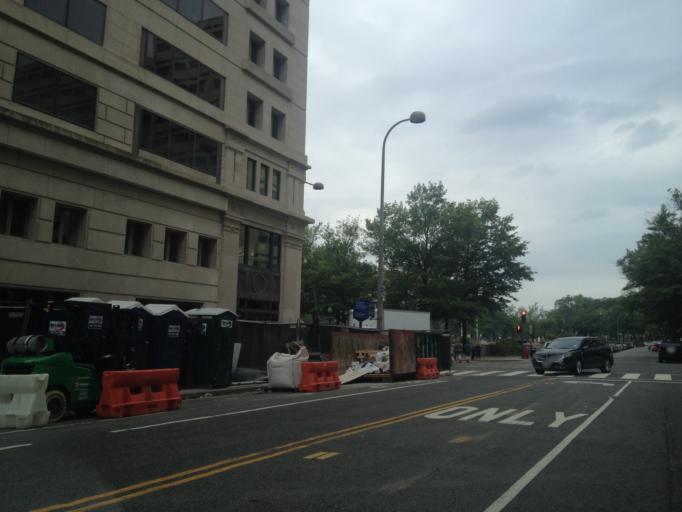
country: US
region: Washington, D.C.
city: Washington, D.C.
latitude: 38.8961
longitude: -77.0291
